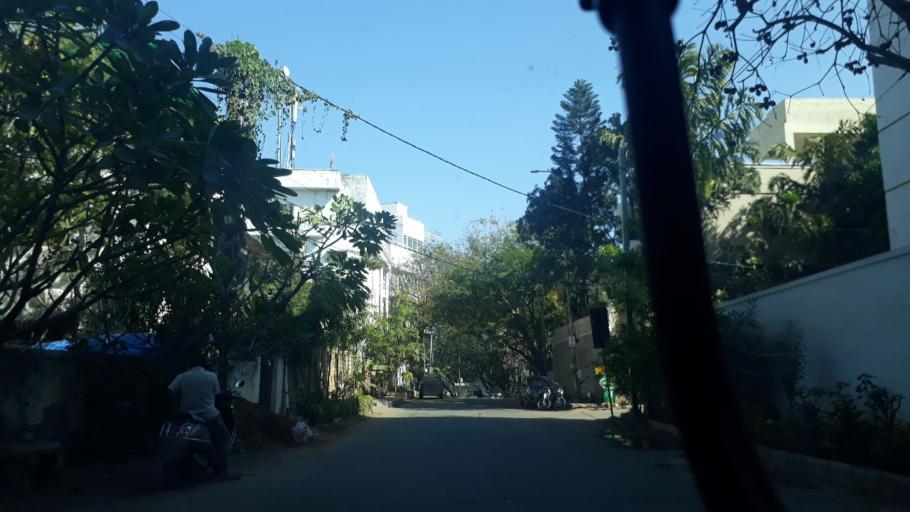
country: IN
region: Telangana
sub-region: Rangareddi
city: Kukatpalli
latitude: 17.4221
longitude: 78.4012
